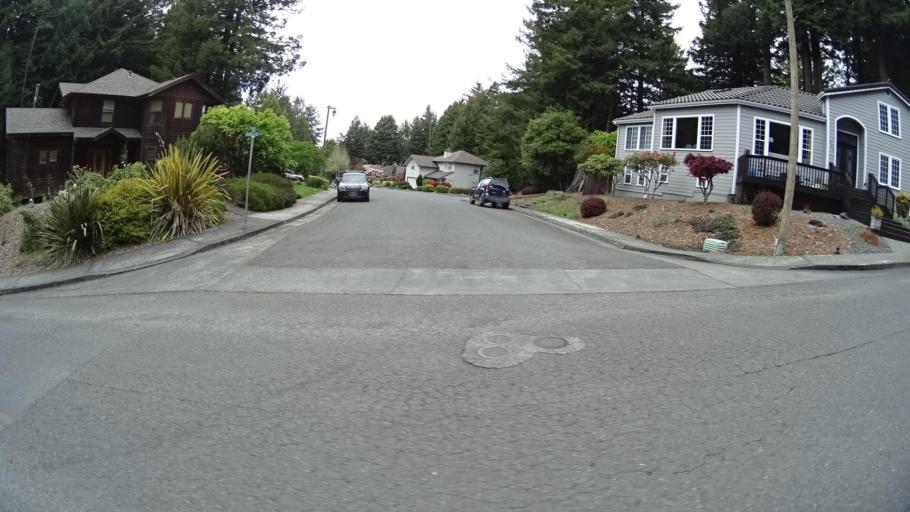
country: US
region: California
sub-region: Humboldt County
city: Arcata
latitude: 40.8885
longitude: -124.0754
